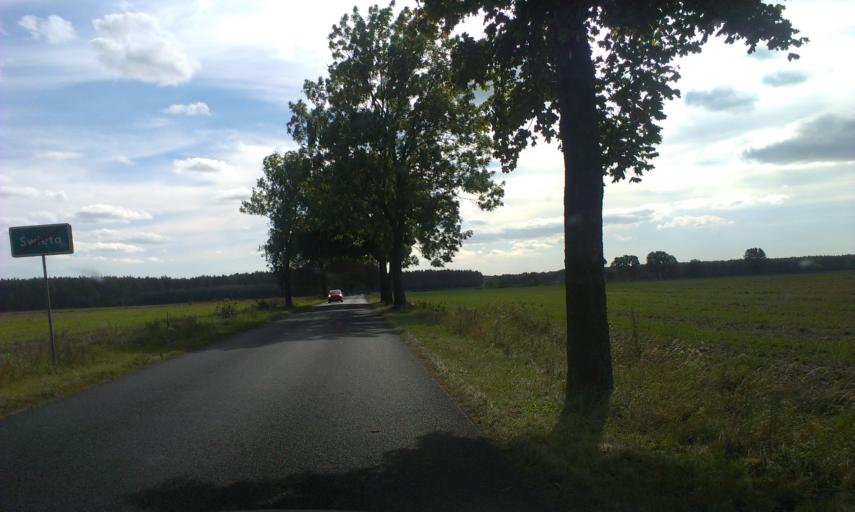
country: PL
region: Greater Poland Voivodeship
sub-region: Powiat zlotowski
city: Zlotow
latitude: 53.3259
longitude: 17.0892
